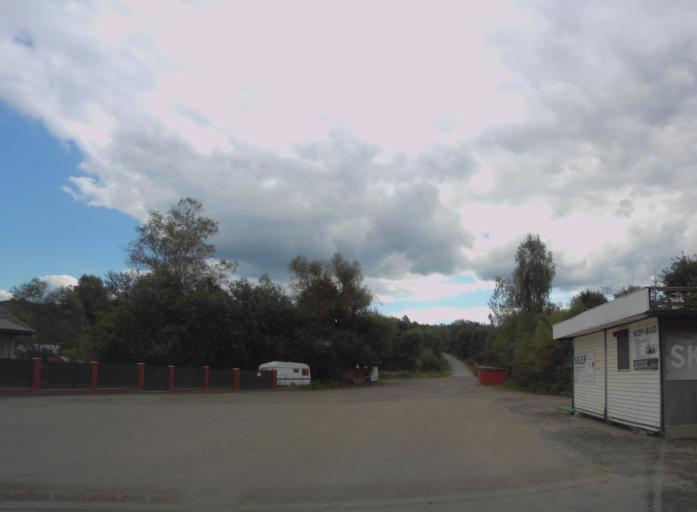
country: PL
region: Subcarpathian Voivodeship
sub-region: Powiat leski
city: Polanczyk
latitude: 49.3142
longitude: 22.5074
